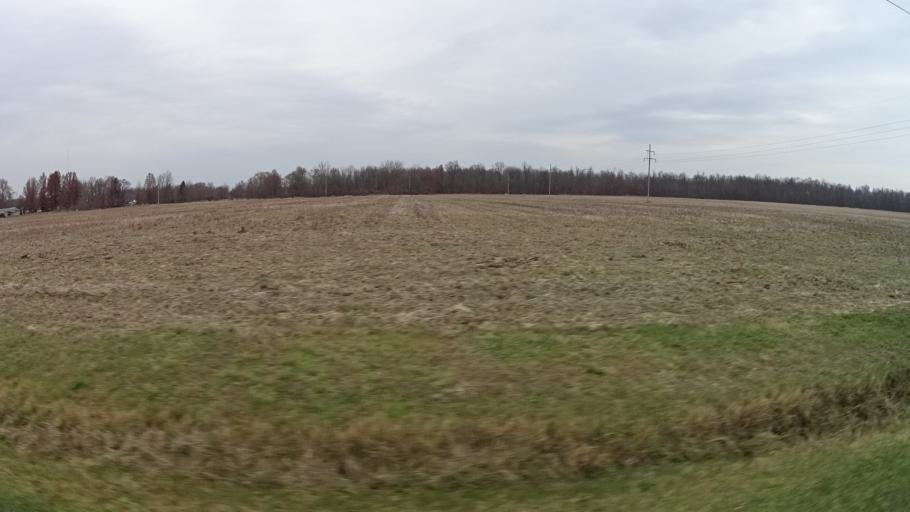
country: US
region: Ohio
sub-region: Lorain County
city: Wellington
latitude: 41.1544
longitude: -82.1661
